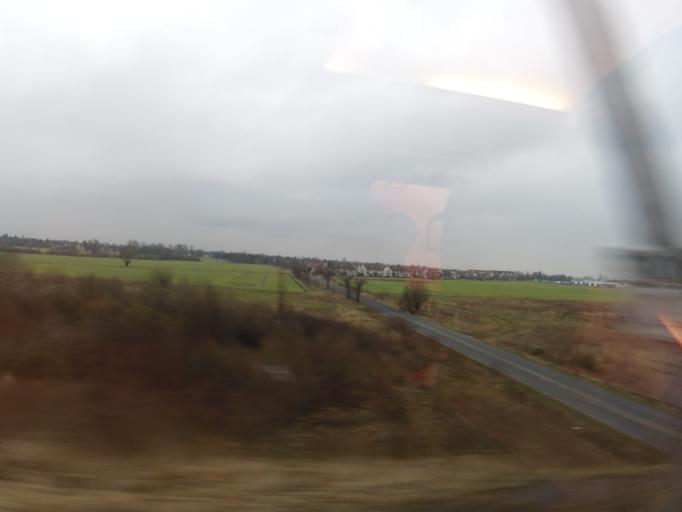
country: DE
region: Saxony
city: Rackwitz
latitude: 51.4078
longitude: 12.3759
